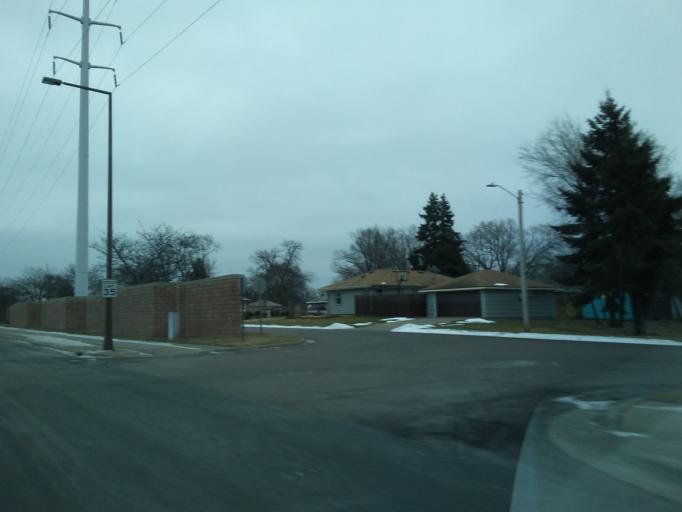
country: US
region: Minnesota
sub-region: Hennepin County
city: Richfield
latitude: 44.8596
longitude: -93.2729
